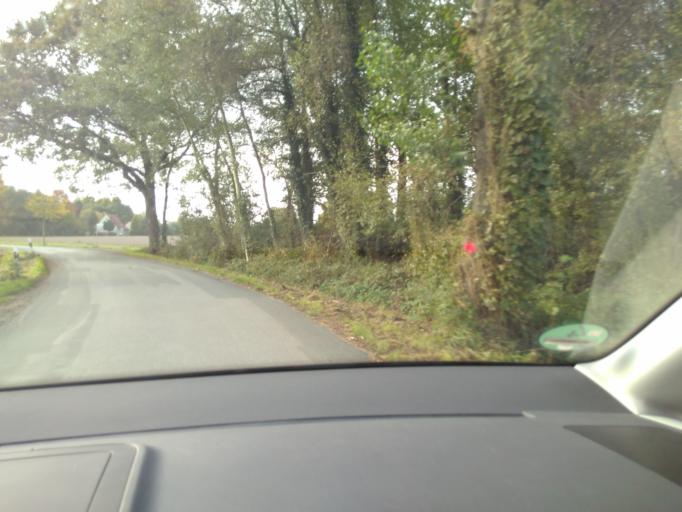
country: DE
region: North Rhine-Westphalia
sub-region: Regierungsbezirk Detmold
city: Verl
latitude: 51.8627
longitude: 8.4912
